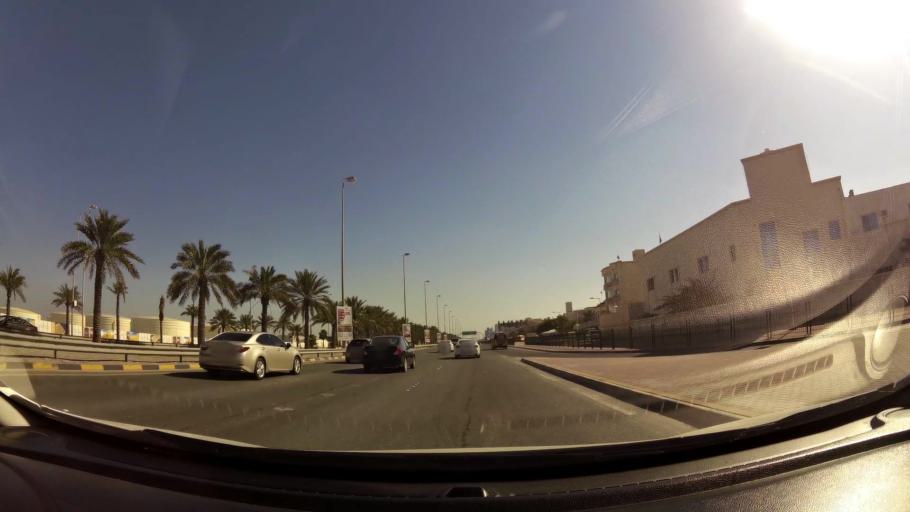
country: BH
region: Muharraq
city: Al Hadd
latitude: 26.2337
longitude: 50.6575
